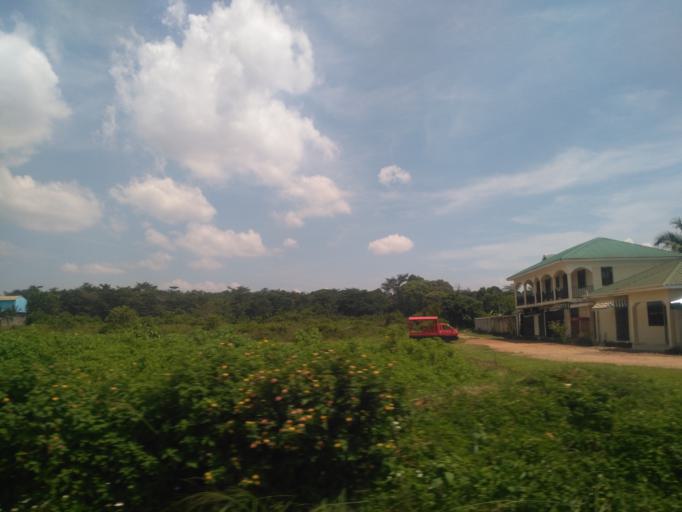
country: UG
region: Central Region
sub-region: Wakiso District
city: Entebbe
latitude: 0.0736
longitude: 32.4823
